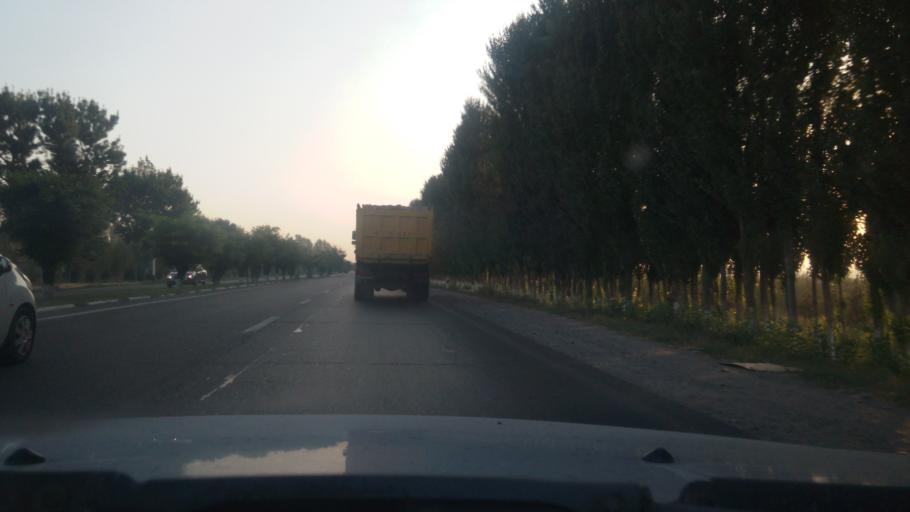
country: UZ
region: Toshkent
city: Yangiyul
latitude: 41.1696
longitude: 69.0639
